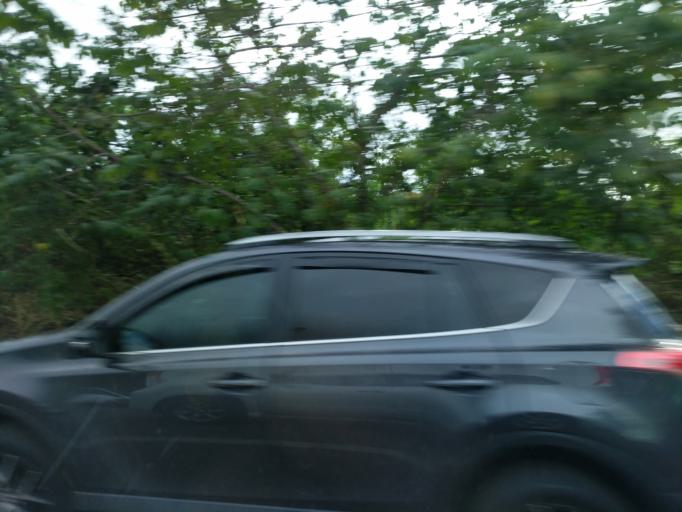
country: PR
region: Coamo
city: Coamo
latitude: 18.0799
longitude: -66.3831
